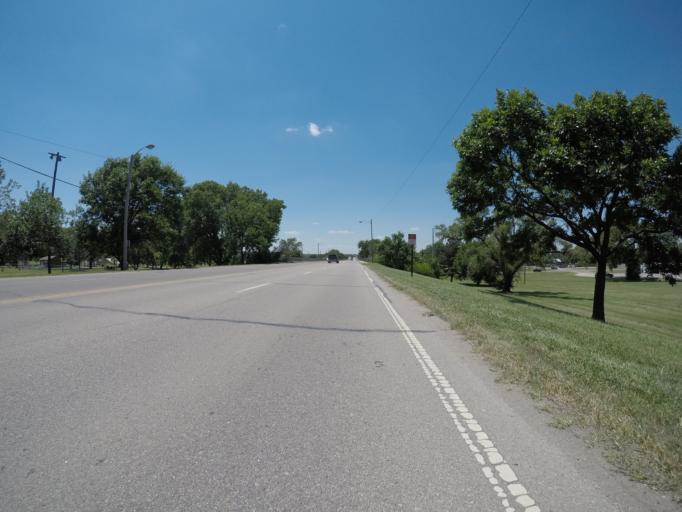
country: US
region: Kansas
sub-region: Geary County
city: Junction City
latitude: 39.0283
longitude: -96.8149
